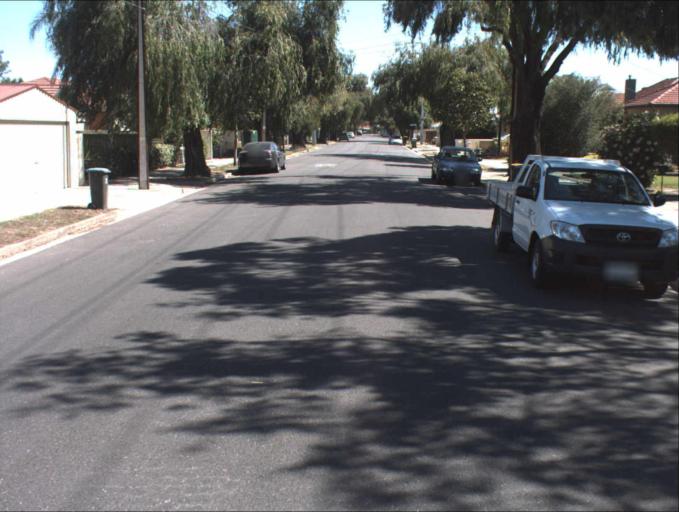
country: AU
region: South Australia
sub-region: Port Adelaide Enfield
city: Birkenhead
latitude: -34.8190
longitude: 138.4971
